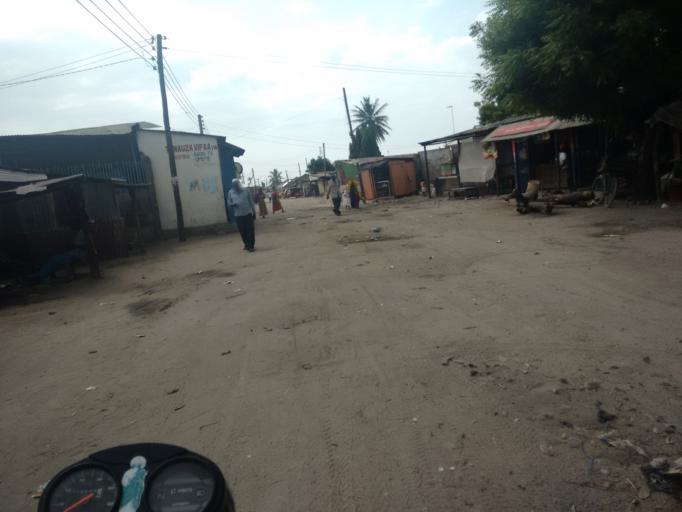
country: TZ
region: Dar es Salaam
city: Dar es Salaam
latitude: -6.8602
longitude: 39.2484
